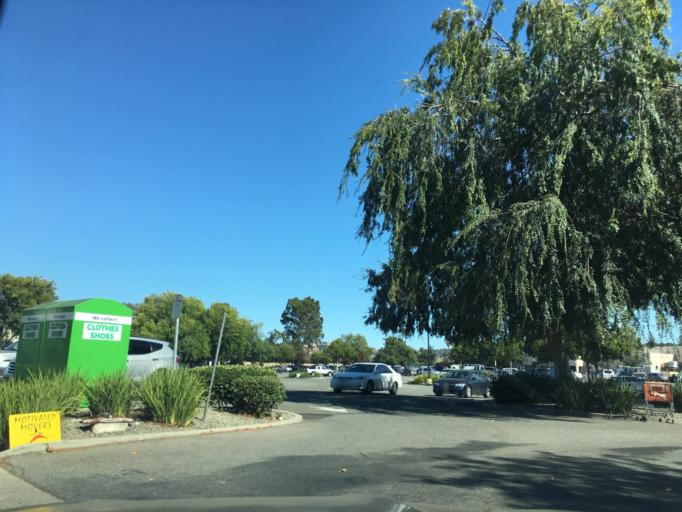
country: US
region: California
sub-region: Santa Clara County
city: Seven Trees
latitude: 37.2503
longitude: -121.8633
